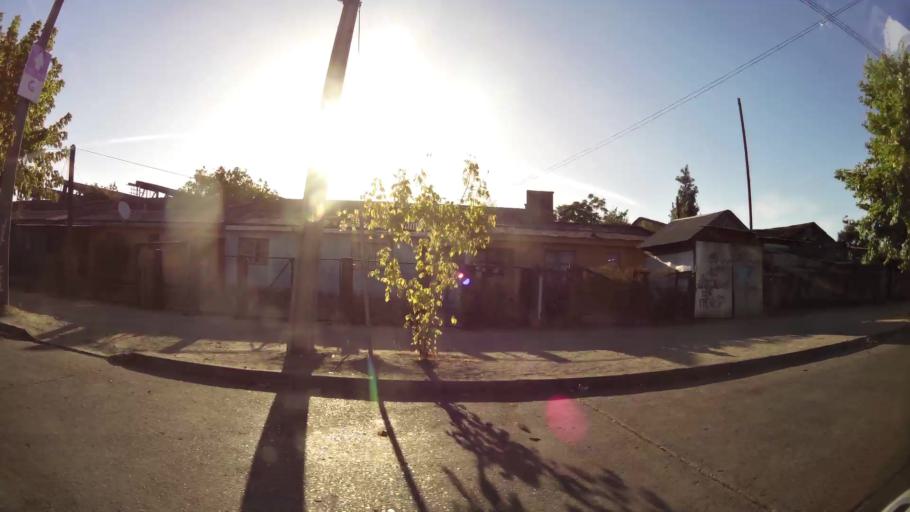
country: CL
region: Maule
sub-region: Provincia de Talca
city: Talca
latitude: -35.4352
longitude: -71.6485
